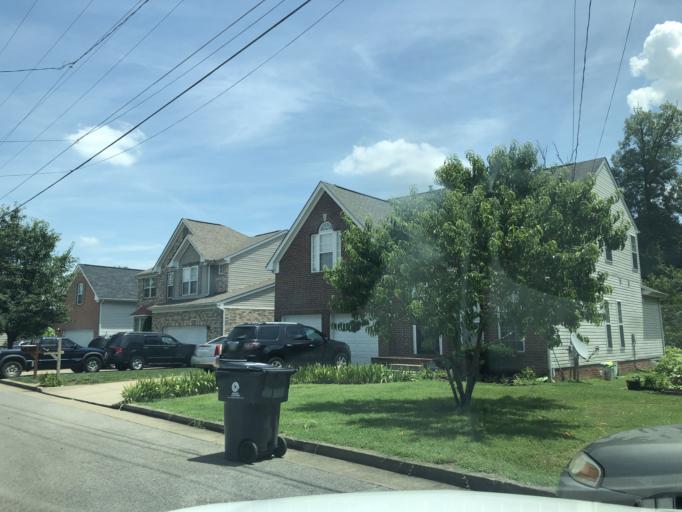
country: US
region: Tennessee
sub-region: Rutherford County
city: La Vergne
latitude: 36.0177
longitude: -86.6482
